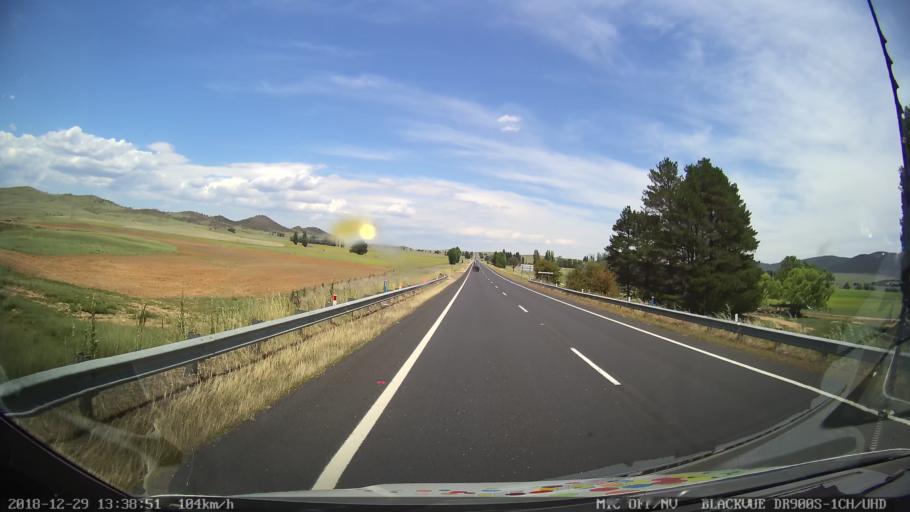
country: AU
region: New South Wales
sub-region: Cooma-Monaro
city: Cooma
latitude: -36.0047
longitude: 149.1438
